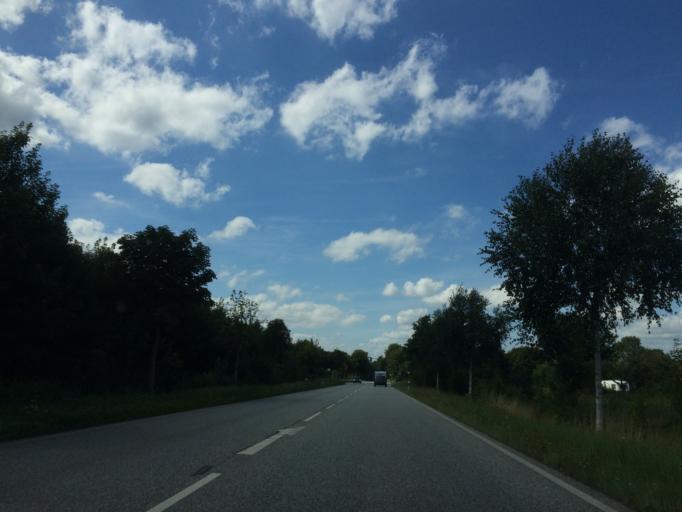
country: DE
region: Schleswig-Holstein
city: Bosdorf
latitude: 54.1389
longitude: 10.4911
